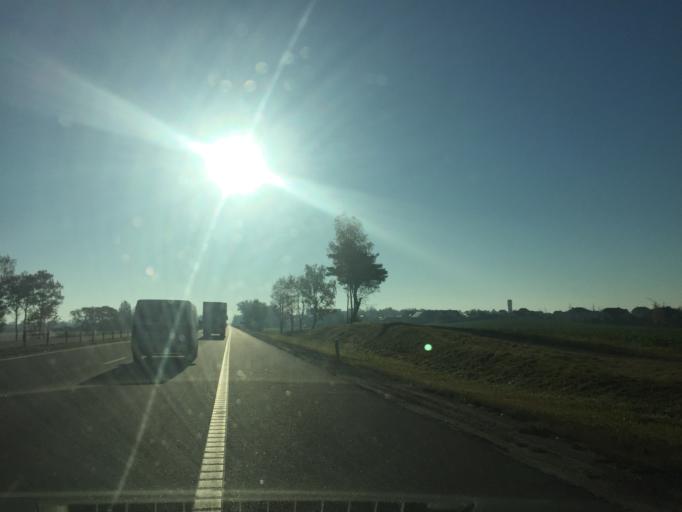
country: BY
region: Minsk
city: Luhavaya Slabada
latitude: 53.7881
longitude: 27.8280
